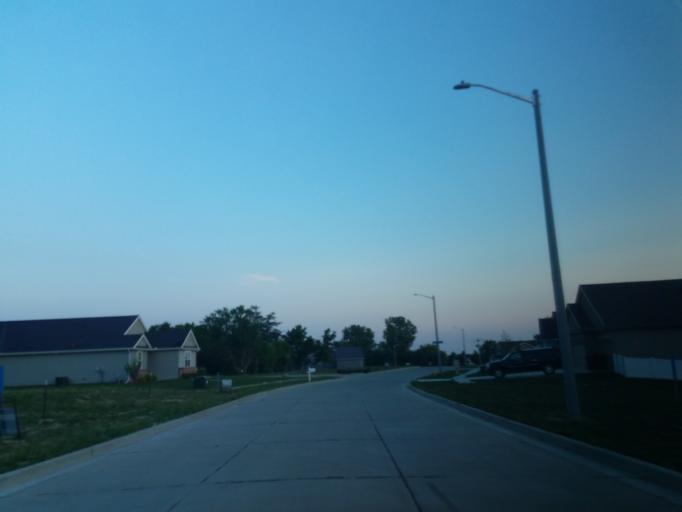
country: US
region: Illinois
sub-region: McLean County
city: Bloomington
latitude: 40.4461
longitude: -89.0083
